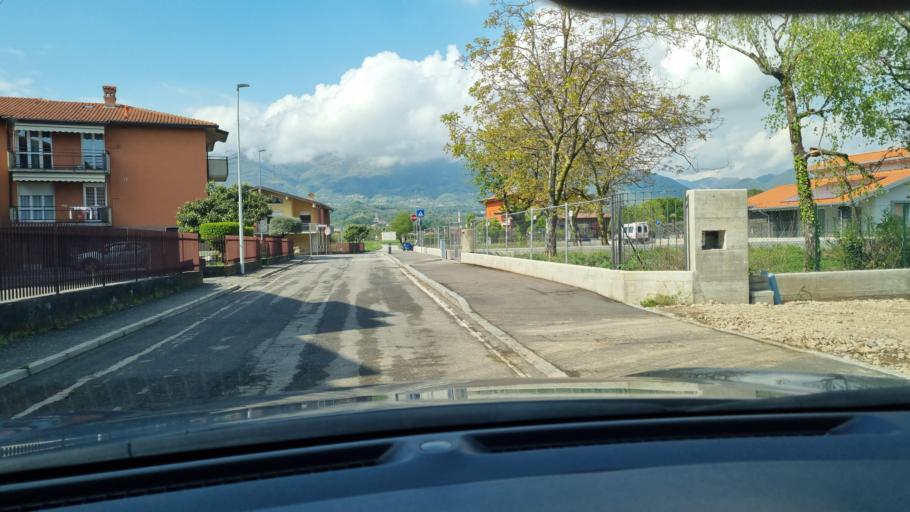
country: IT
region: Lombardy
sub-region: Provincia di Bergamo
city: Mapello
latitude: 45.7116
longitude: 9.5526
